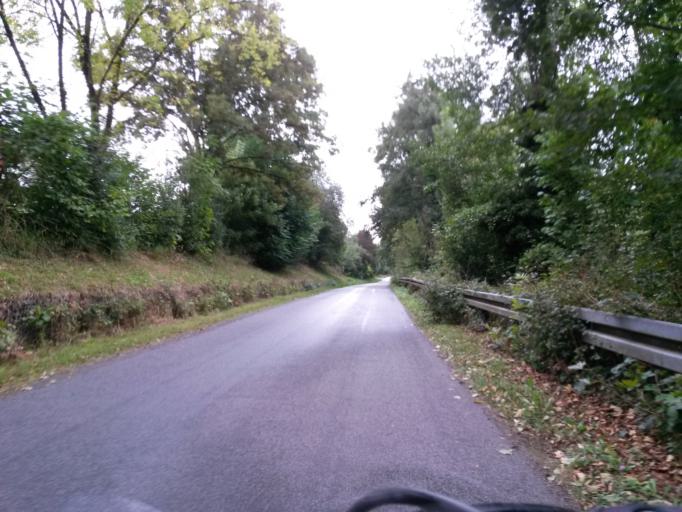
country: DE
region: Baden-Wuerttemberg
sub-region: Karlsruhe Region
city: Konigsbach-Stein
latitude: 48.9266
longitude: 8.5705
